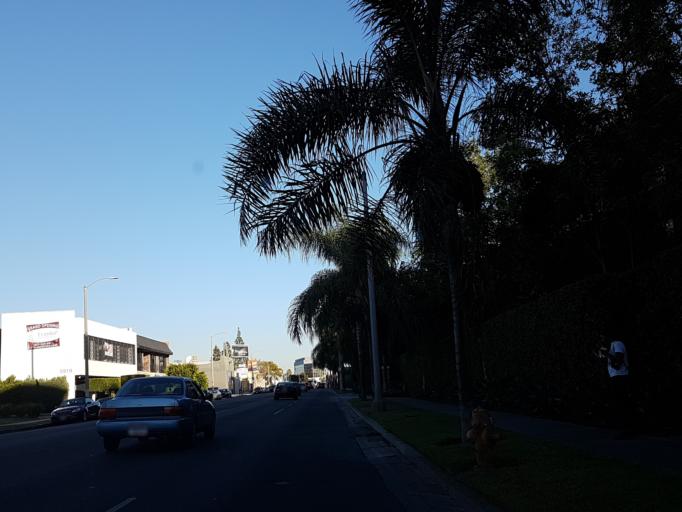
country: US
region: California
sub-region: Los Angeles County
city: West Hollywood
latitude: 34.0697
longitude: -118.3501
